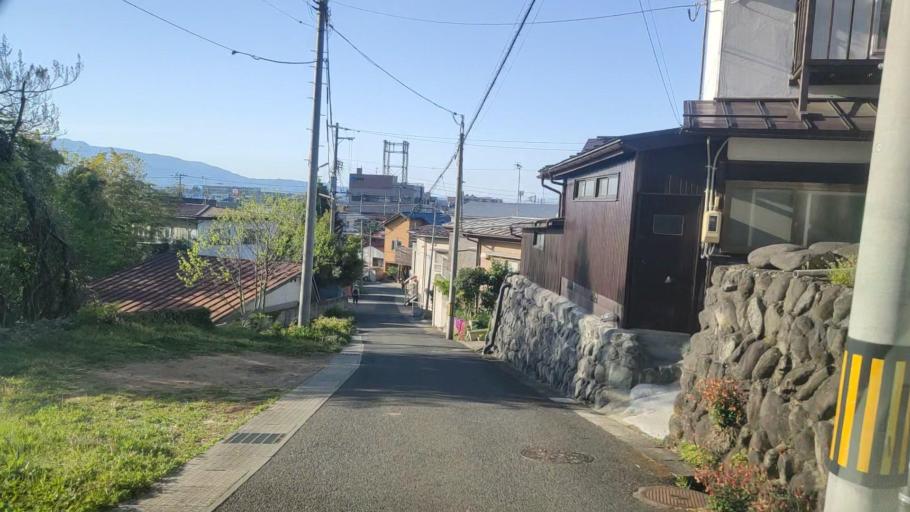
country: JP
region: Yamagata
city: Tendo
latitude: 38.3581
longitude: 140.3754
